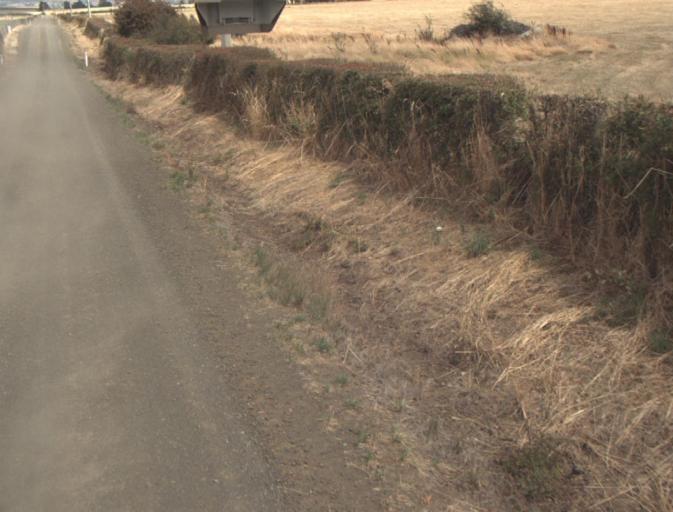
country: AU
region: Tasmania
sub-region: Northern Midlands
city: Evandale
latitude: -41.5172
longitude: 147.2922
